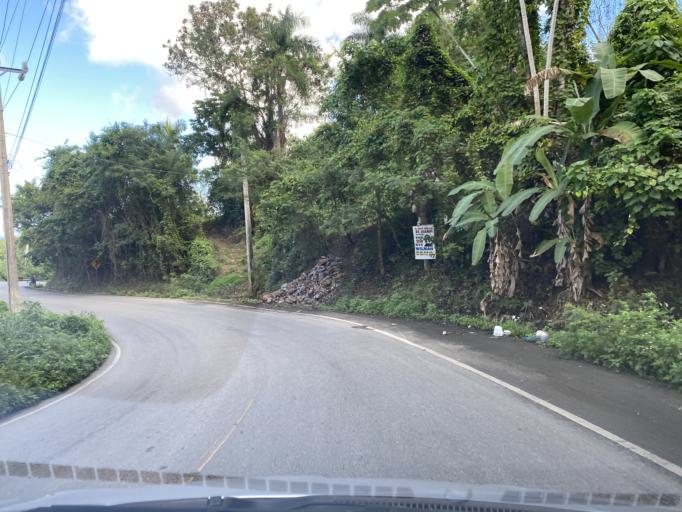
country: DO
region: Samana
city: Las Terrenas
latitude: 19.2871
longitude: -69.5493
